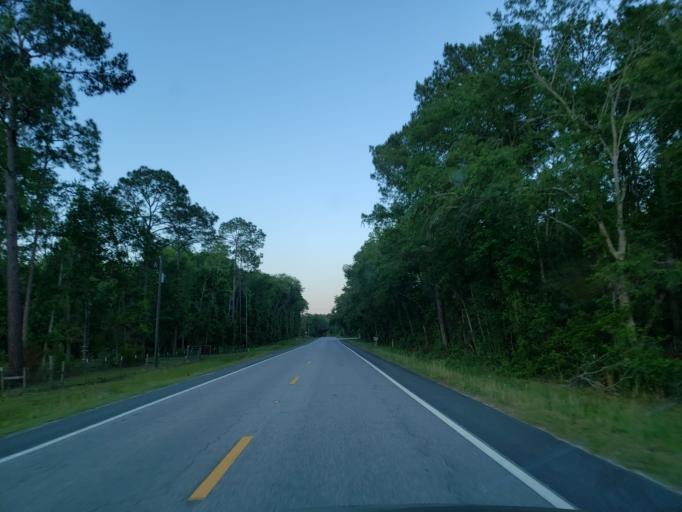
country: US
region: Florida
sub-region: Hamilton County
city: Jasper
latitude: 30.5566
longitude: -83.0931
